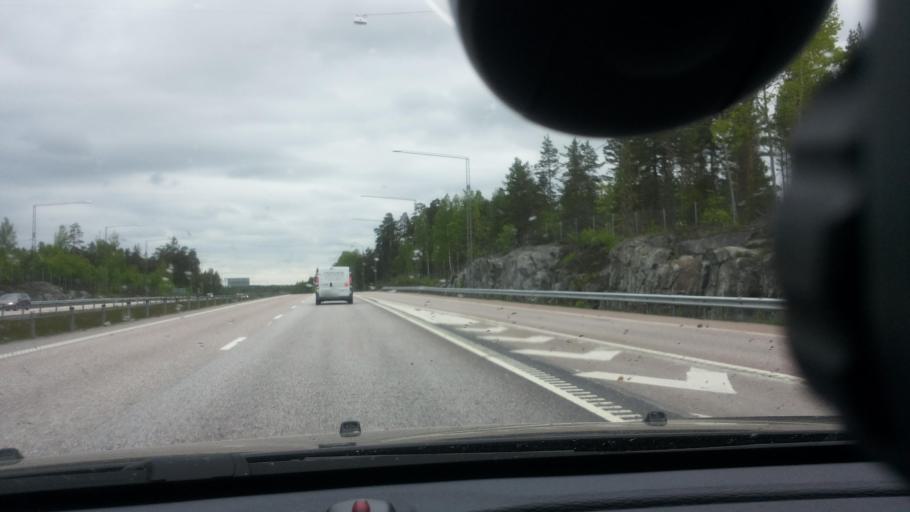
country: SE
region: Stockholm
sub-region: Sigtuna Kommun
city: Rosersberg
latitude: 59.6233
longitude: 17.9013
